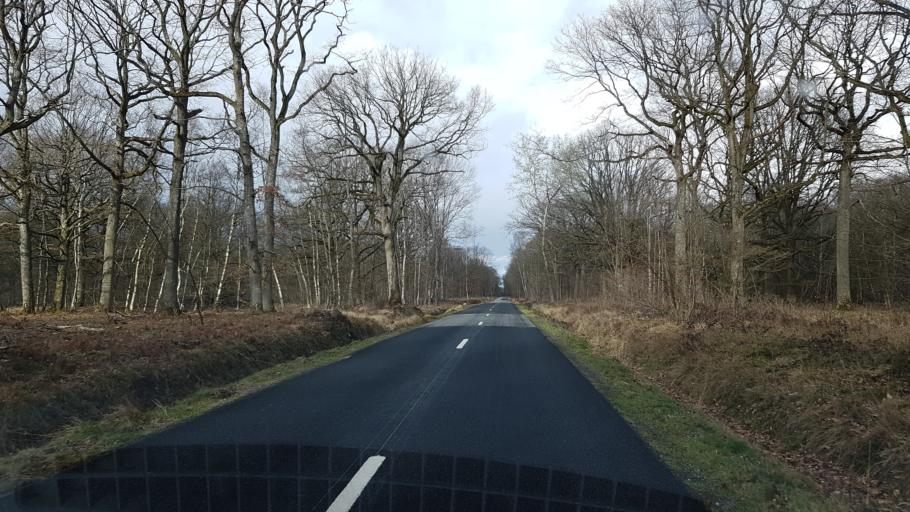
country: FR
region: Ile-de-France
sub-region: Departement des Yvelines
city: Saint-Arnoult-en-Yvelines
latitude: 48.6236
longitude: 1.9235
